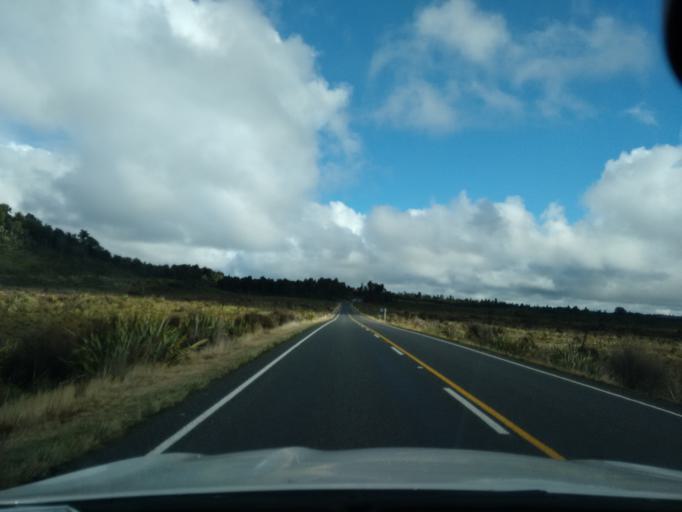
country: NZ
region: Manawatu-Wanganui
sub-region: Ruapehu District
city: Waiouru
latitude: -39.2274
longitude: 175.3957
